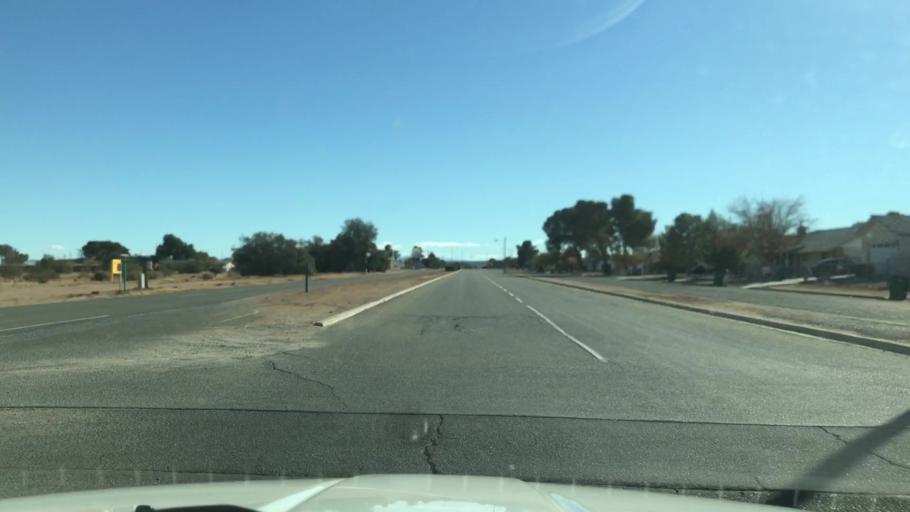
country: US
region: California
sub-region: Kern County
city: California City
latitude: 35.1295
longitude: -117.9858
